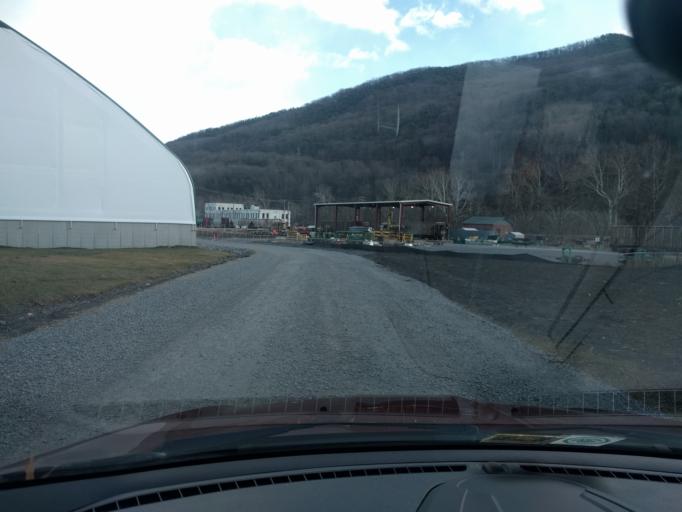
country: US
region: Virginia
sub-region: Alleghany County
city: Clifton Forge
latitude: 37.8092
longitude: -79.8397
